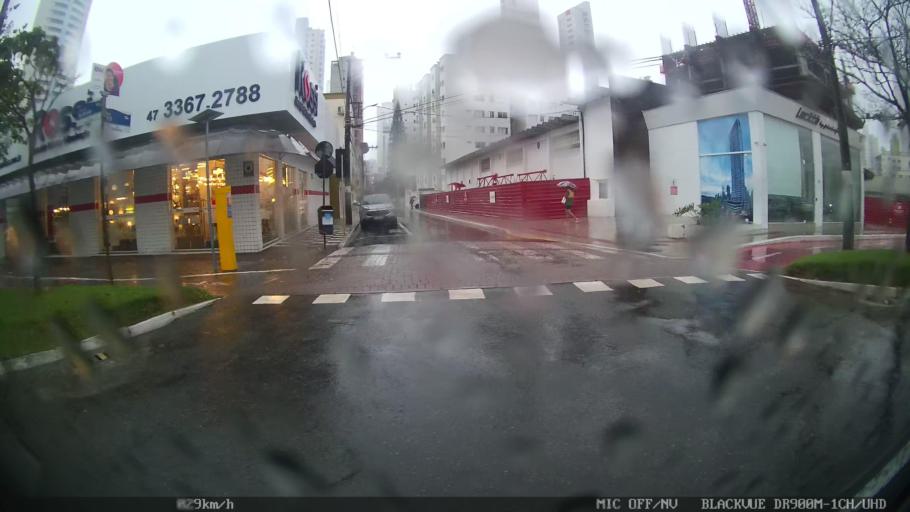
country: BR
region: Santa Catarina
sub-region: Balneario Camboriu
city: Balneario Camboriu
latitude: -26.9848
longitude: -48.6398
